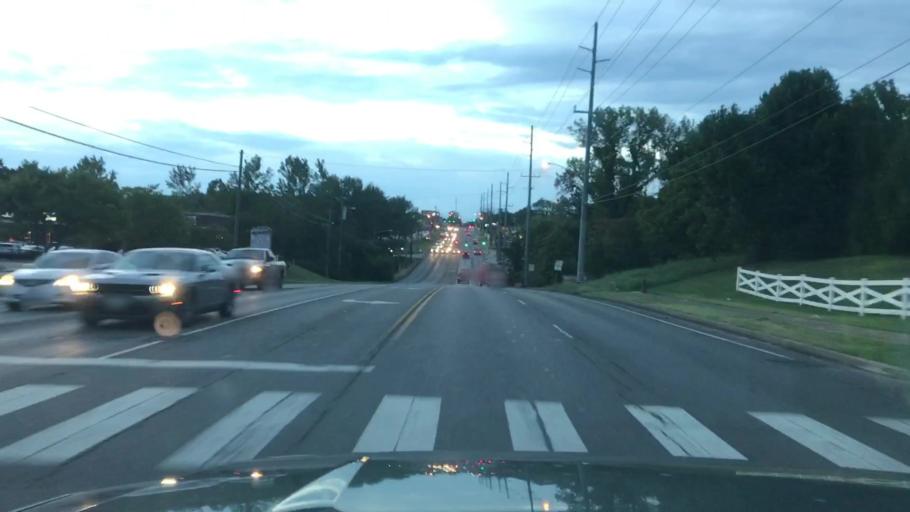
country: US
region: Tennessee
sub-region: Rutherford County
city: La Vergne
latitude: 36.0891
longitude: -86.6500
